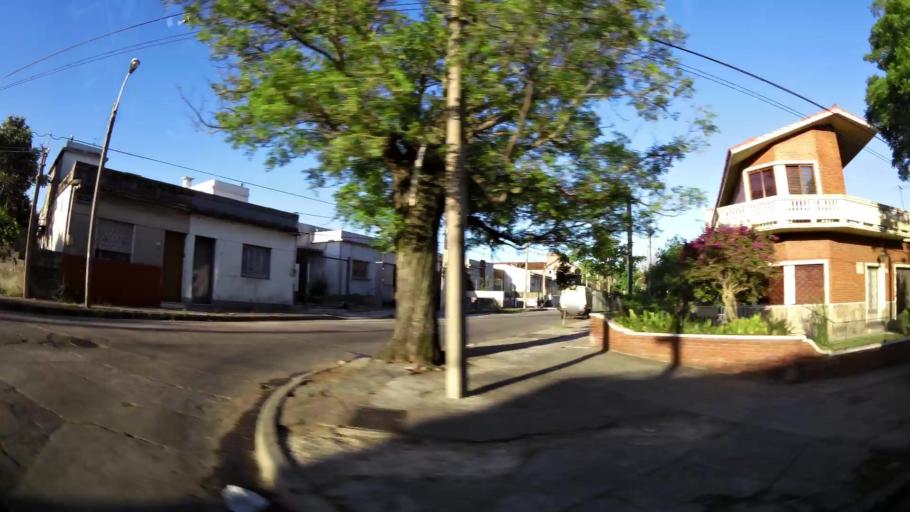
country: UY
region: Montevideo
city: Montevideo
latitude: -34.8481
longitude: -56.2052
